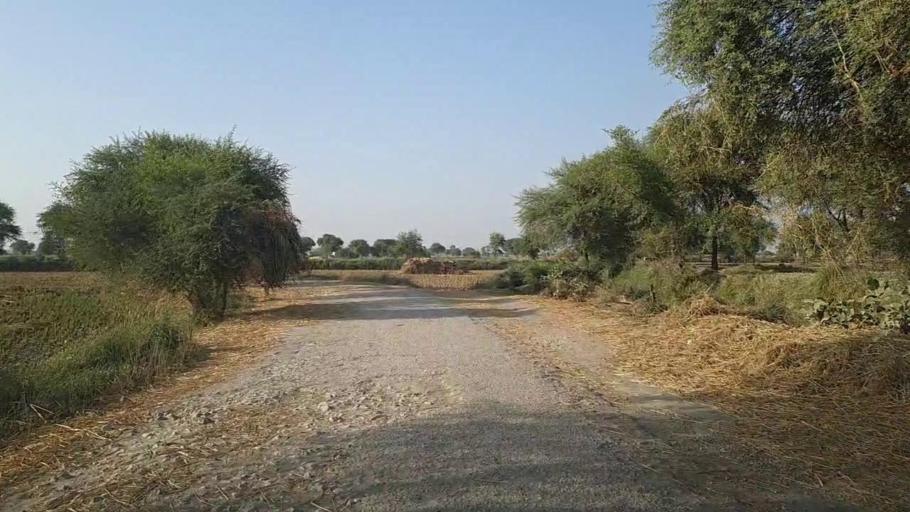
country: PK
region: Sindh
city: Kashmor
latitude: 28.4066
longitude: 69.4139
